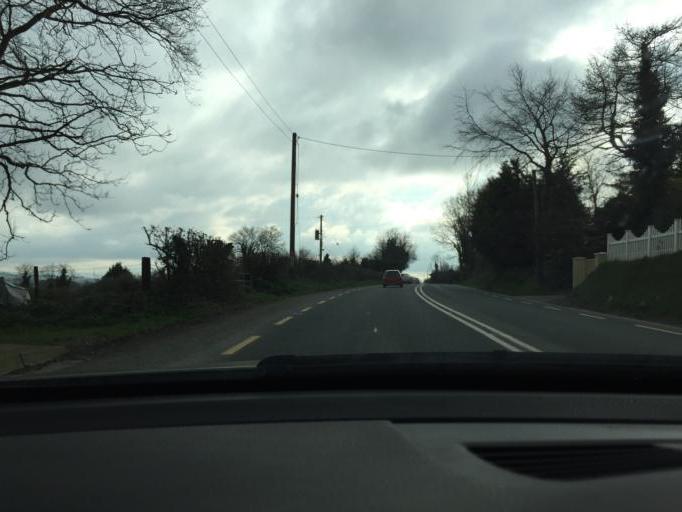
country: IE
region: Leinster
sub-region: Wicklow
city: Blessington
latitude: 53.2051
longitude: -6.4960
